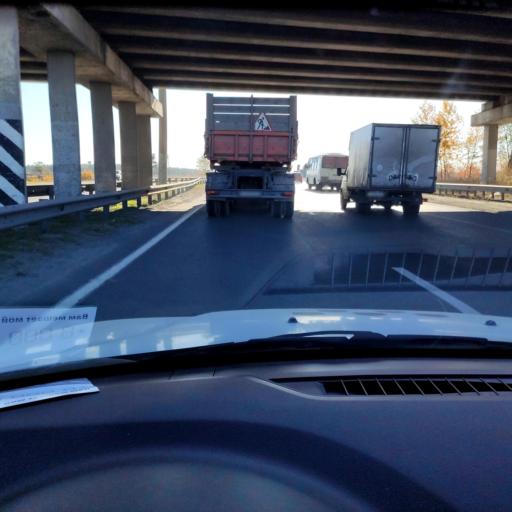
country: RU
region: Samara
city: Zhigulevsk
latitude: 53.5178
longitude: 49.5348
